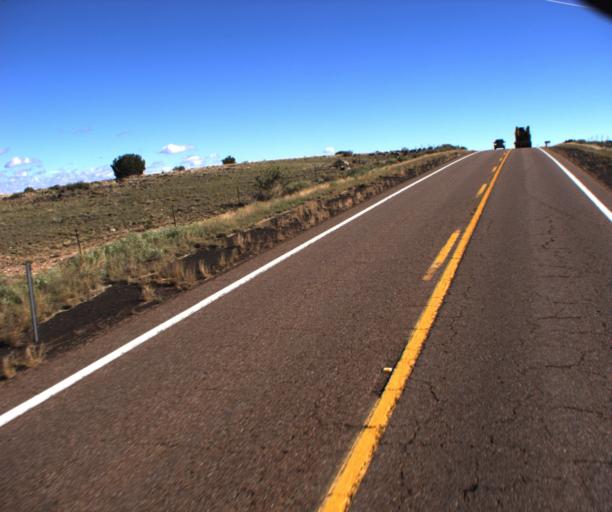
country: US
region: Arizona
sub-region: Apache County
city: Saint Johns
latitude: 34.4942
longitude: -109.5121
